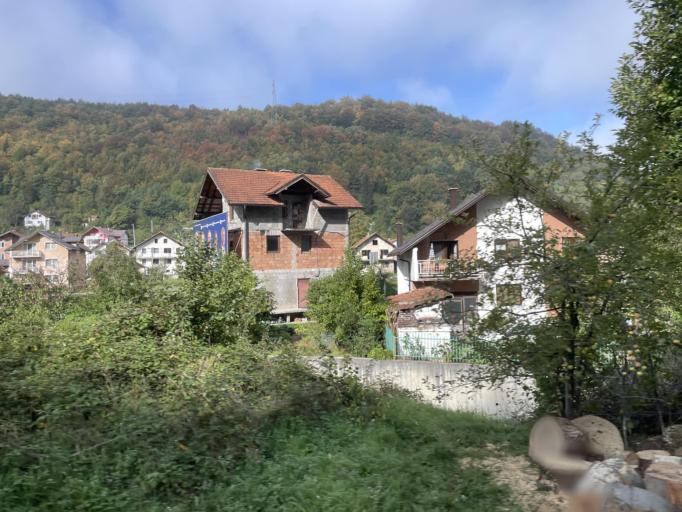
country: BA
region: Federation of Bosnia and Herzegovina
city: Hadzici
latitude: 43.8185
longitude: 18.1947
